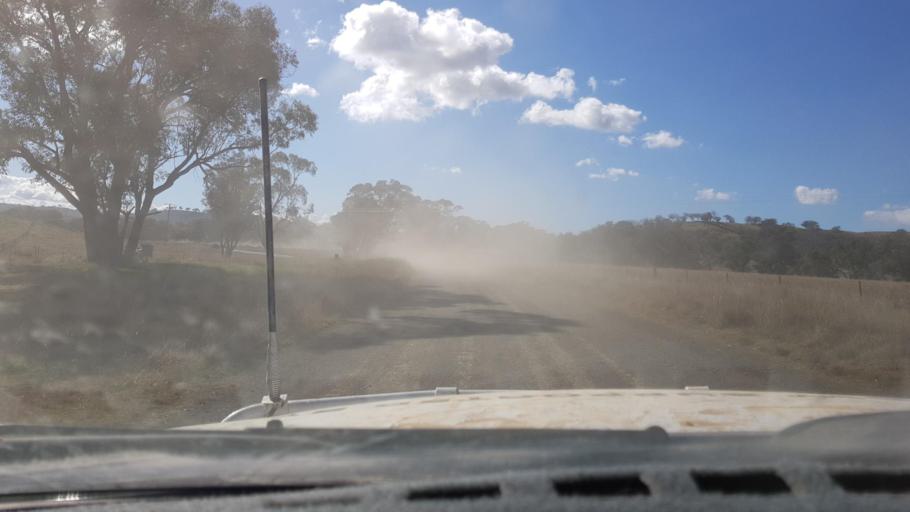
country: AU
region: New South Wales
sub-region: Narrabri
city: Blair Athol
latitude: -30.4762
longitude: 150.4435
